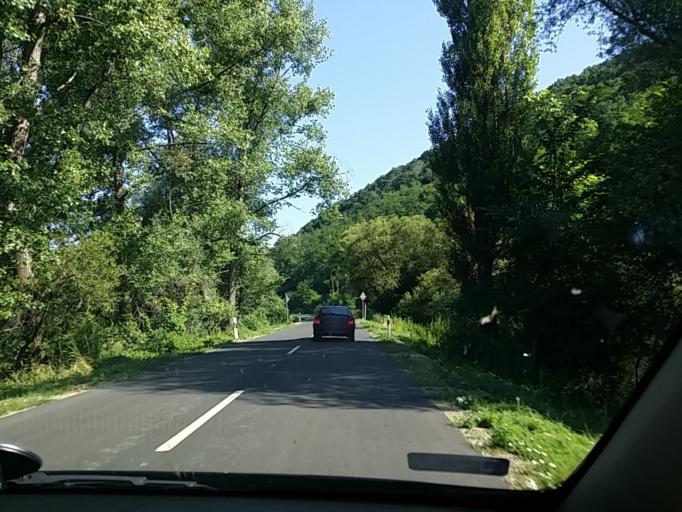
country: HU
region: Nograd
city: Szecseny
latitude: 48.1955
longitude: 19.5298
